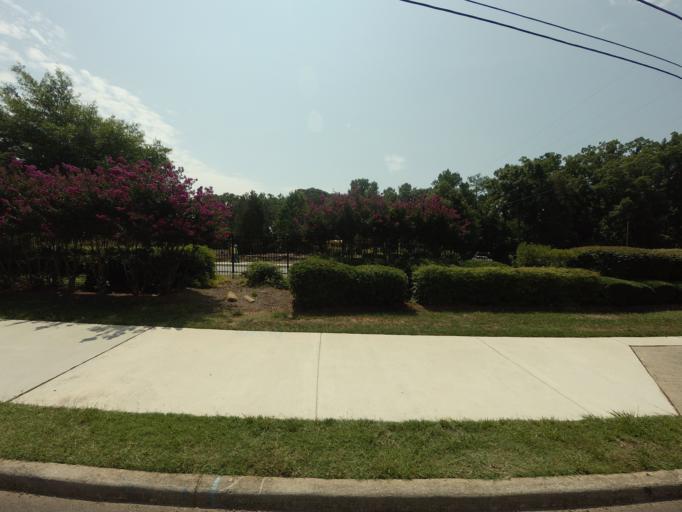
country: US
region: Georgia
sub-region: Fulton County
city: Alpharetta
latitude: 34.0185
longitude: -84.2781
